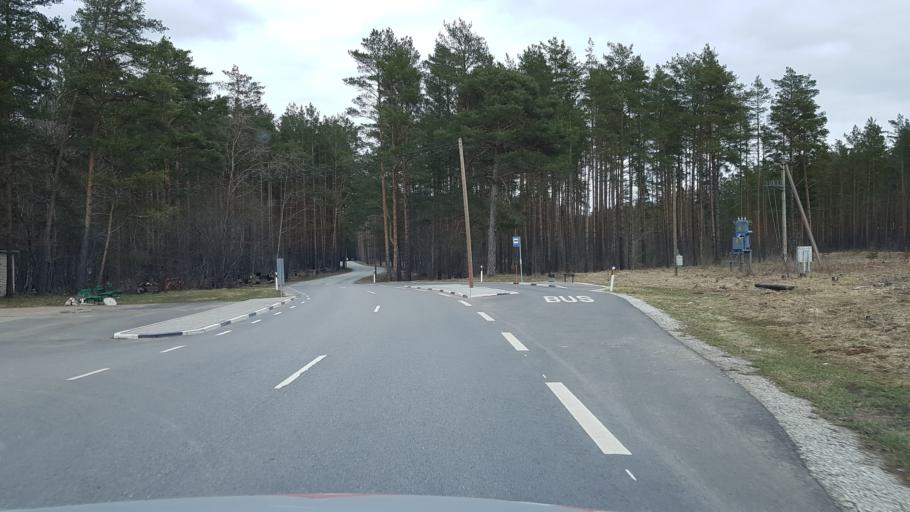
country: EE
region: Ida-Virumaa
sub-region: Narva-Joesuu linn
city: Narva-Joesuu
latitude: 59.4197
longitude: 28.1066
